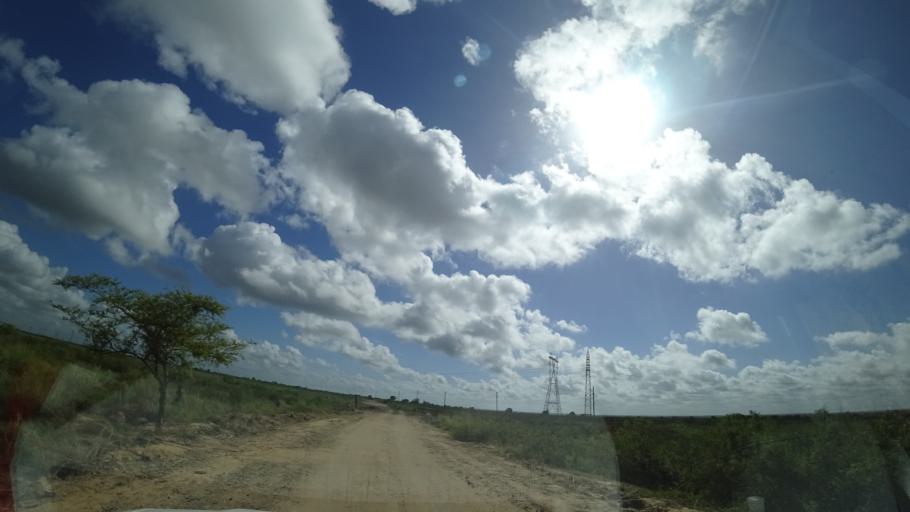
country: MZ
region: Sofala
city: Dondo
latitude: -19.4614
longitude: 34.5629
